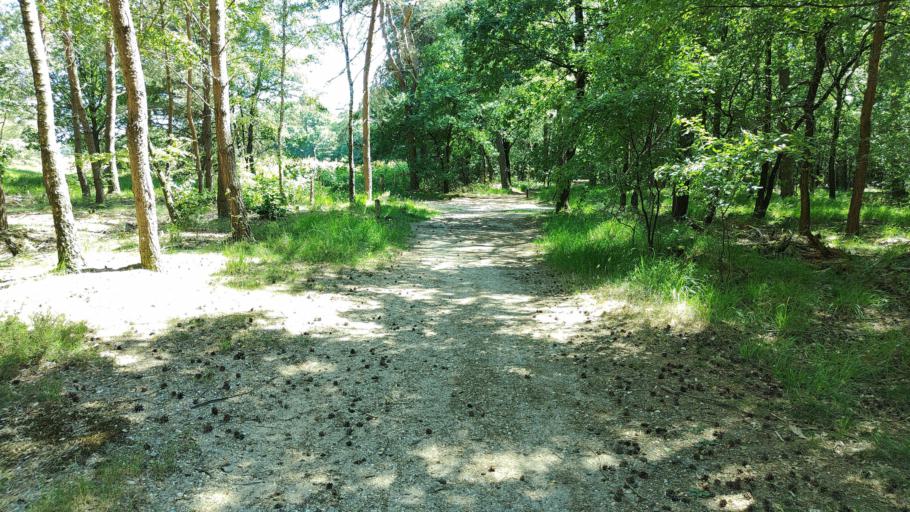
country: NL
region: Gelderland
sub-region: Gemeente Nijmegen
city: Nijmegen
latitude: 51.7897
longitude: 5.8709
